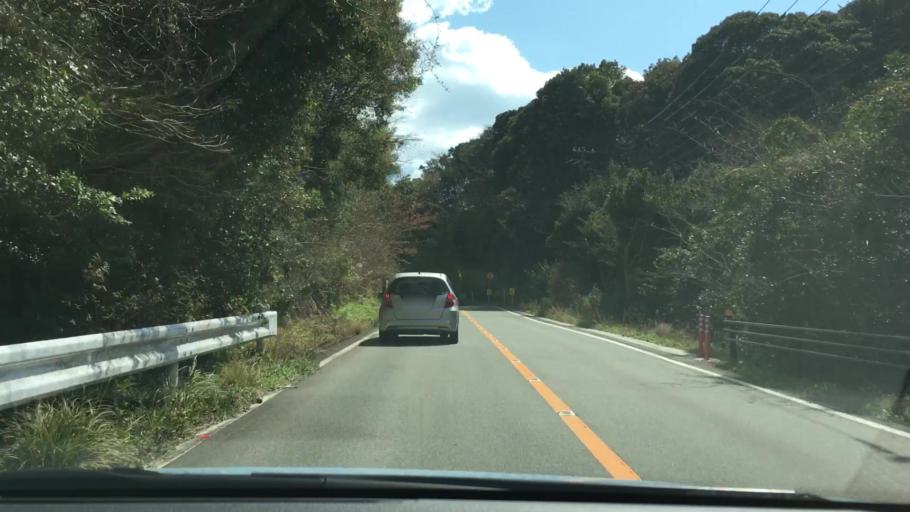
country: JP
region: Mie
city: Toba
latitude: 34.4541
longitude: 136.8656
